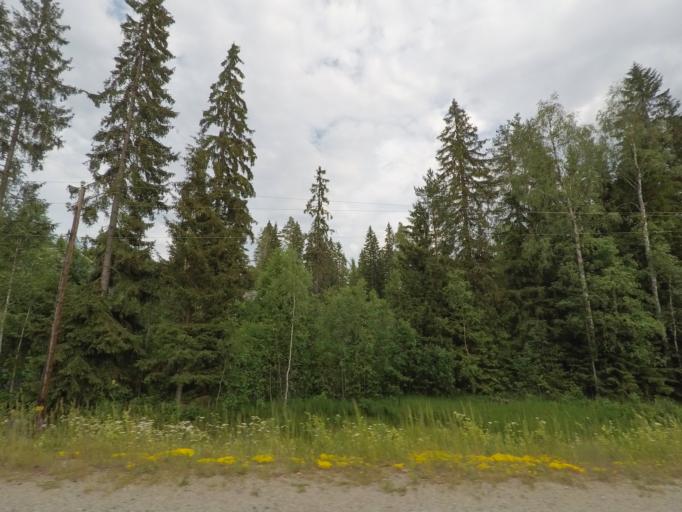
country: FI
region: Paijanne Tavastia
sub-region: Lahti
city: Hollola
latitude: 60.9048
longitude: 25.5408
